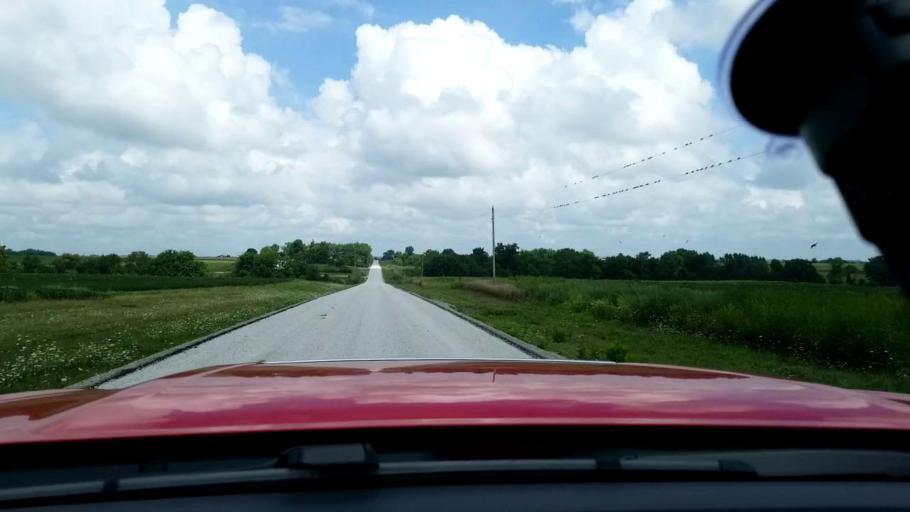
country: US
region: Iowa
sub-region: Decatur County
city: Lamoni
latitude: 40.6290
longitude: -94.0533
